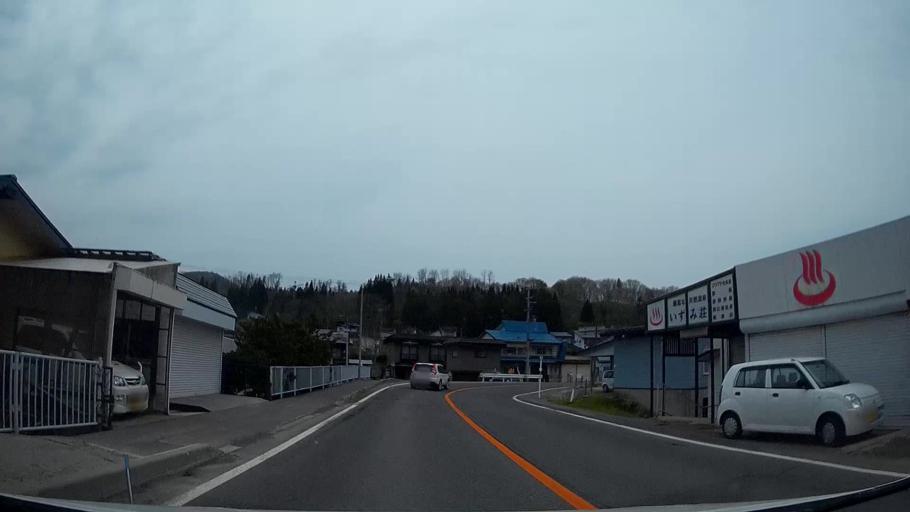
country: JP
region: Akita
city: Hanawa
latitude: 40.2978
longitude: 140.8373
